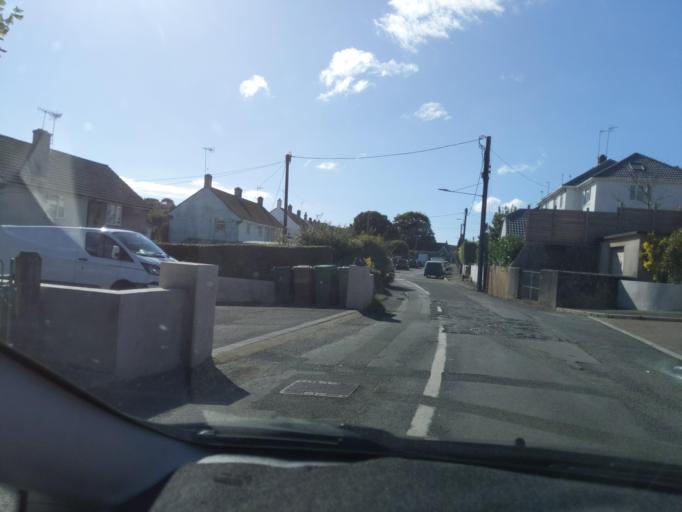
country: GB
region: England
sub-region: Plymouth
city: Plymstock
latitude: 50.3567
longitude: -4.0708
